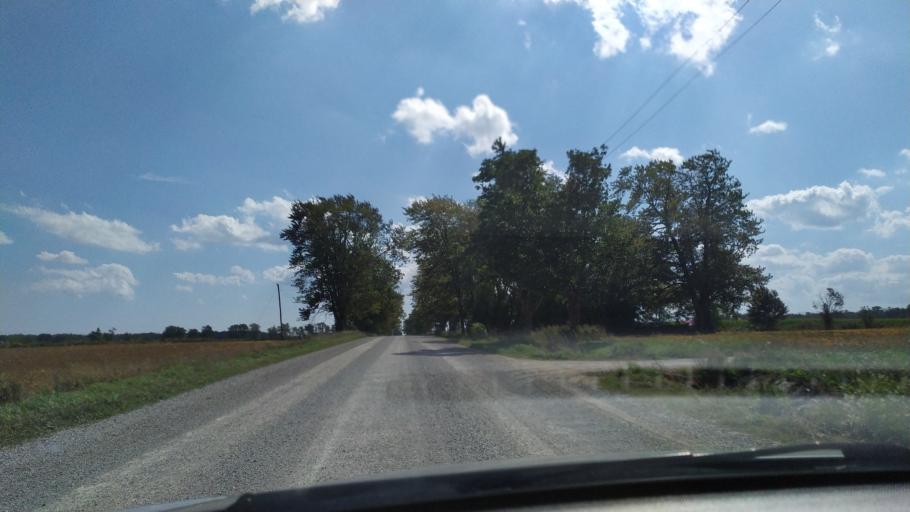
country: CA
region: Ontario
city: Stratford
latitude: 43.2856
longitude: -80.9291
